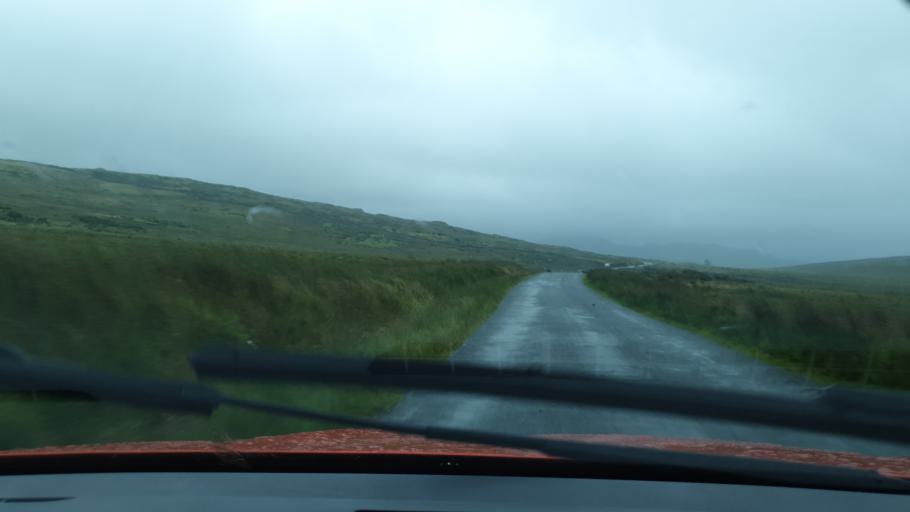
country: GB
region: England
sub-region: Cumbria
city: Millom
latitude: 54.3531
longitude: -3.2582
